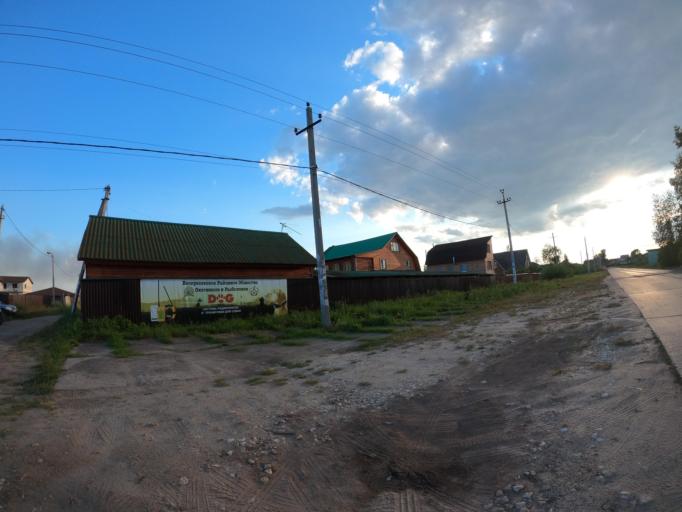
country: RU
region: Moskovskaya
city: Ashitkovo
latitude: 55.4190
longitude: 38.5849
